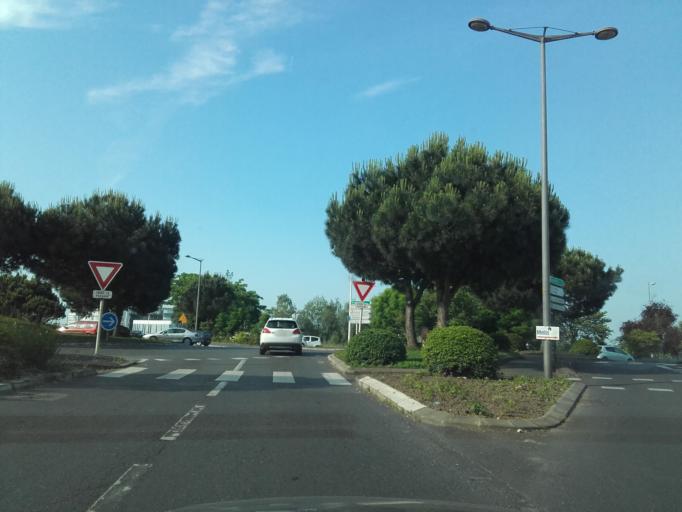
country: FR
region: Centre
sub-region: Departement d'Indre-et-Loire
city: Tours
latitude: 47.3741
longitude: 0.6787
